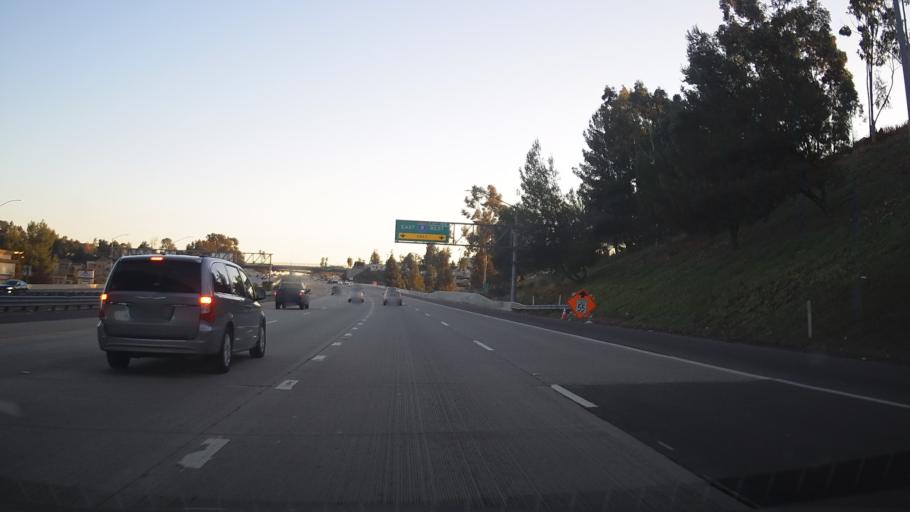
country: US
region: California
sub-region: San Diego County
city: La Mesa
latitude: 32.7869
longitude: -117.0066
